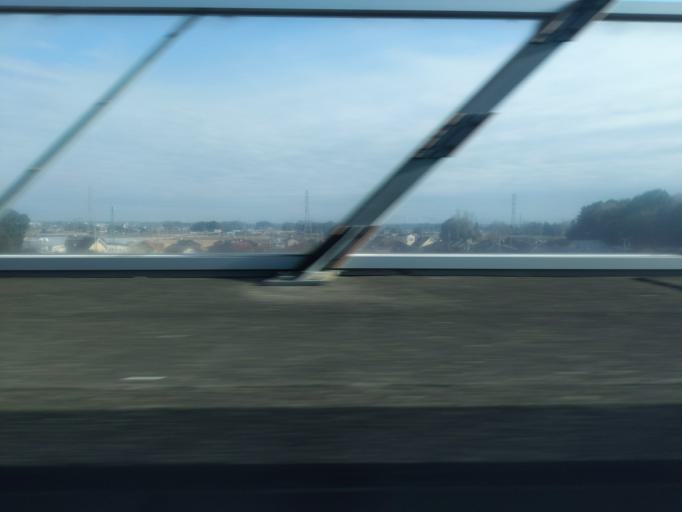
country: JP
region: Tochigi
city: Kaminokawa
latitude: 36.4809
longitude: 139.8748
